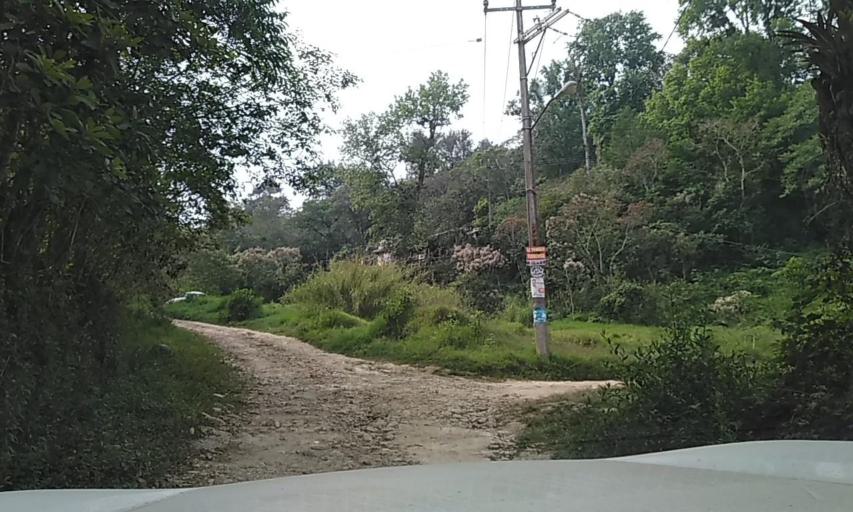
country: MX
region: Veracruz
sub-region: Xalapa
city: Xalapa de Enriquez
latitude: 19.5008
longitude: -96.9195
